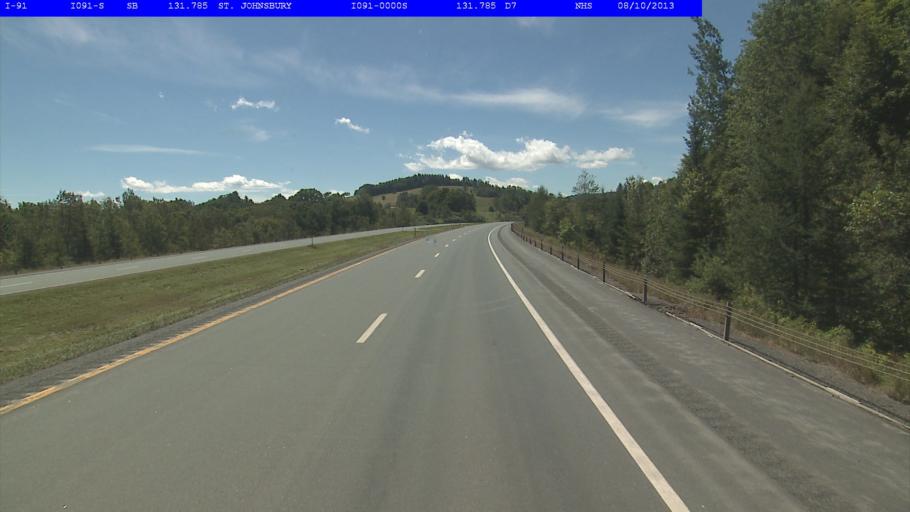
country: US
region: Vermont
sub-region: Caledonia County
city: St Johnsbury
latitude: 44.4426
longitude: -72.0249
